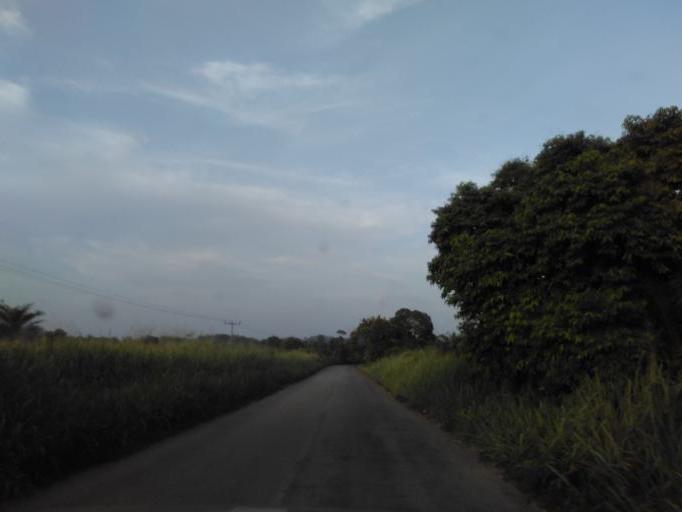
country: GH
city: Bekwai
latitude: 6.5401
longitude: -1.4634
